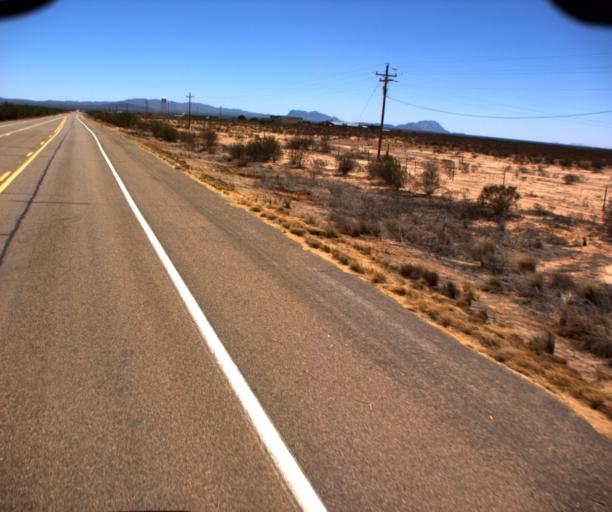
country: US
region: Arizona
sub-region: Pima County
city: Ajo
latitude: 32.1905
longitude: -112.4142
